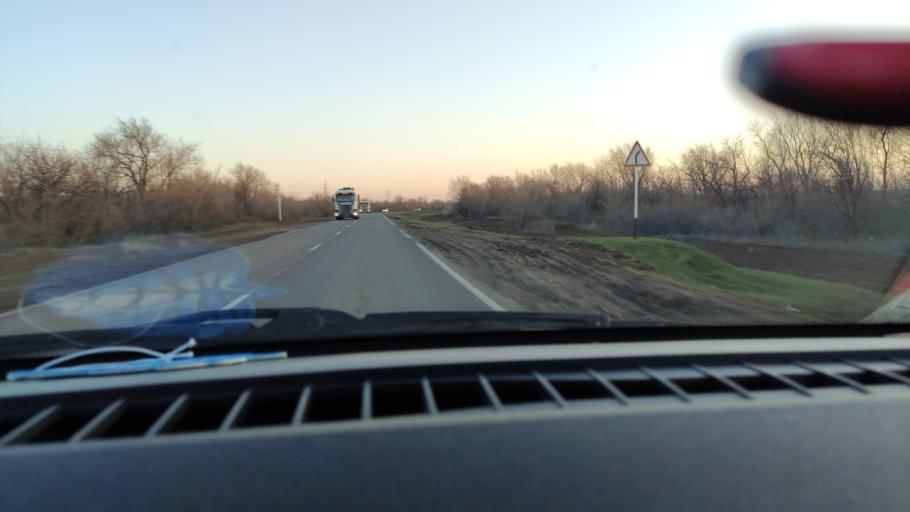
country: RU
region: Saratov
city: Privolzhskiy
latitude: 51.3241
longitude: 46.0290
